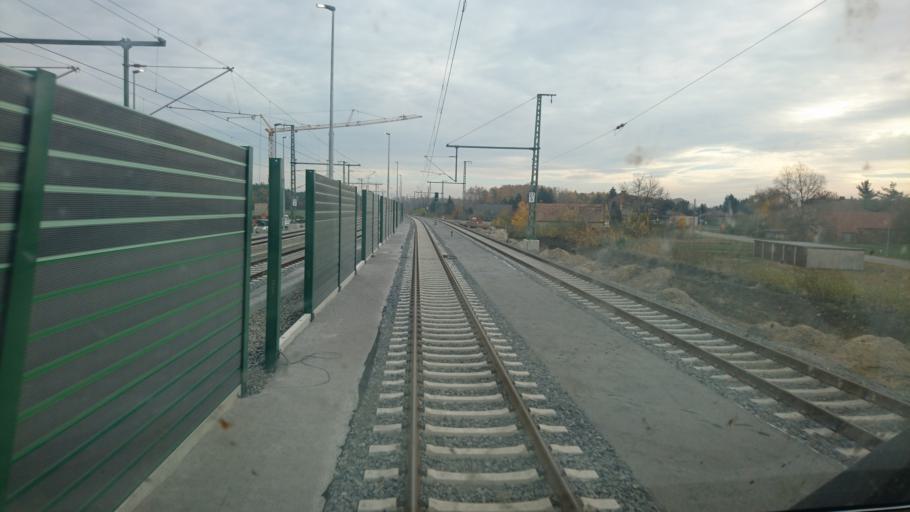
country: DE
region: Saxony
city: Niesky
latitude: 51.2987
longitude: 14.8338
